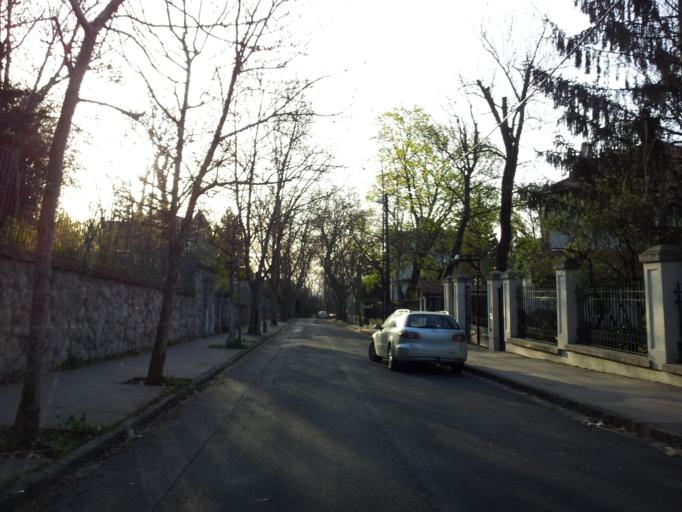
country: HU
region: Budapest
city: Budapest II. keruelet
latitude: 47.5176
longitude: 19.0300
